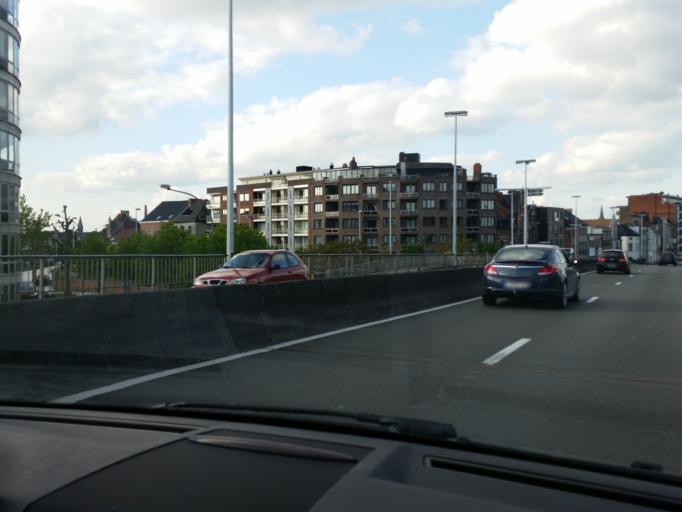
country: BE
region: Flanders
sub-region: Provincie Oost-Vlaanderen
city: Ledeberg
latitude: 51.0426
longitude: 3.7405
